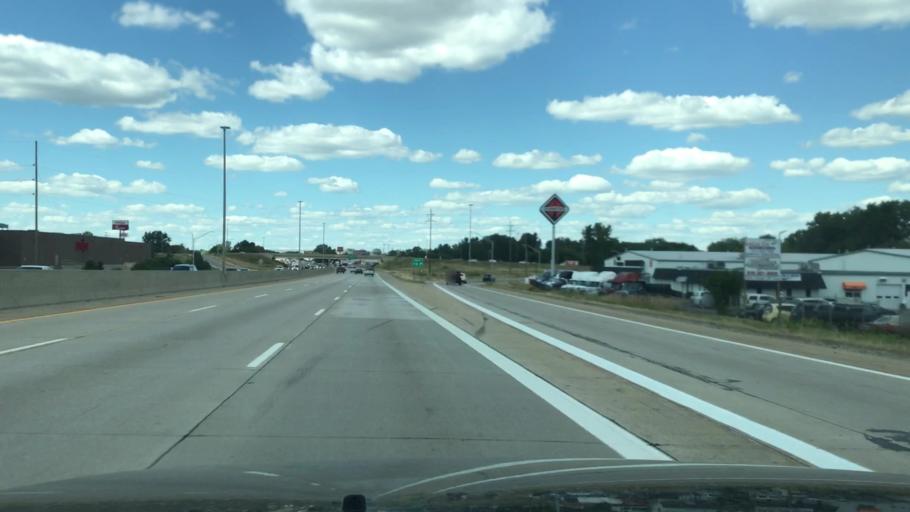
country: US
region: Michigan
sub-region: Kent County
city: Cutlerville
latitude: 42.8618
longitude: -85.6791
